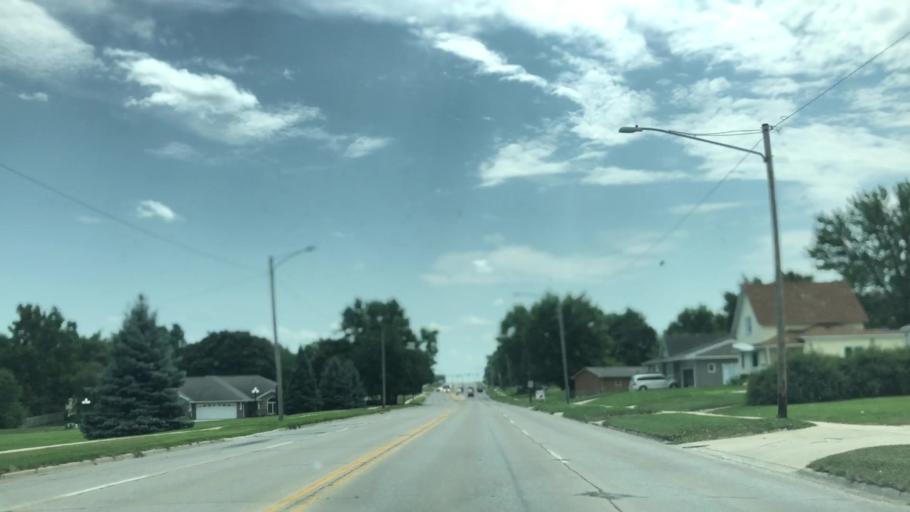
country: US
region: Iowa
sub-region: Marshall County
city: Marshalltown
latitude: 42.0314
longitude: -92.9127
